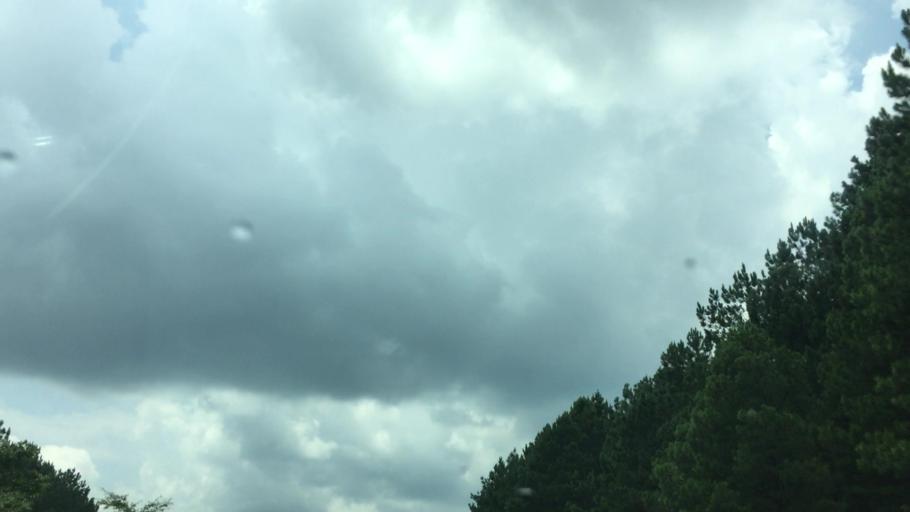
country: US
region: Georgia
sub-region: Fulton County
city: Fairburn
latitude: 33.6090
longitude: -84.6182
